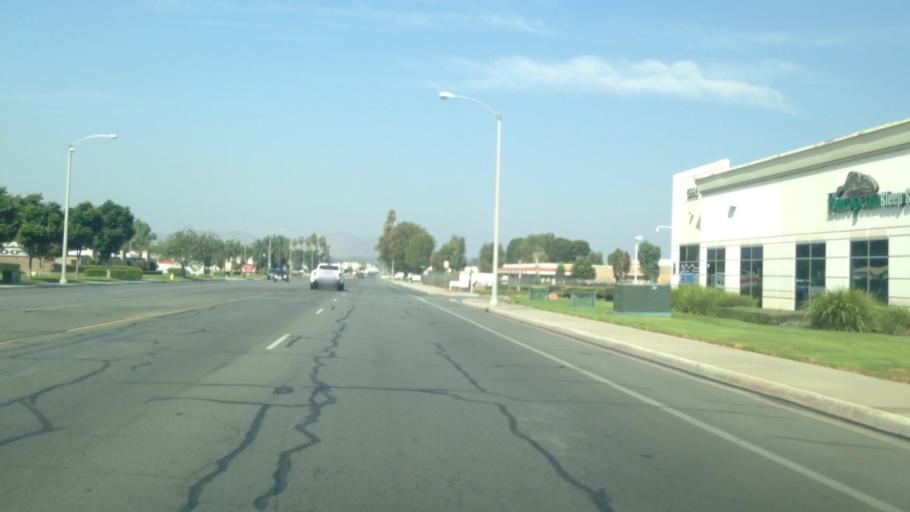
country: US
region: California
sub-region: Riverside County
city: Pedley
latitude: 33.9459
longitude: -117.4469
